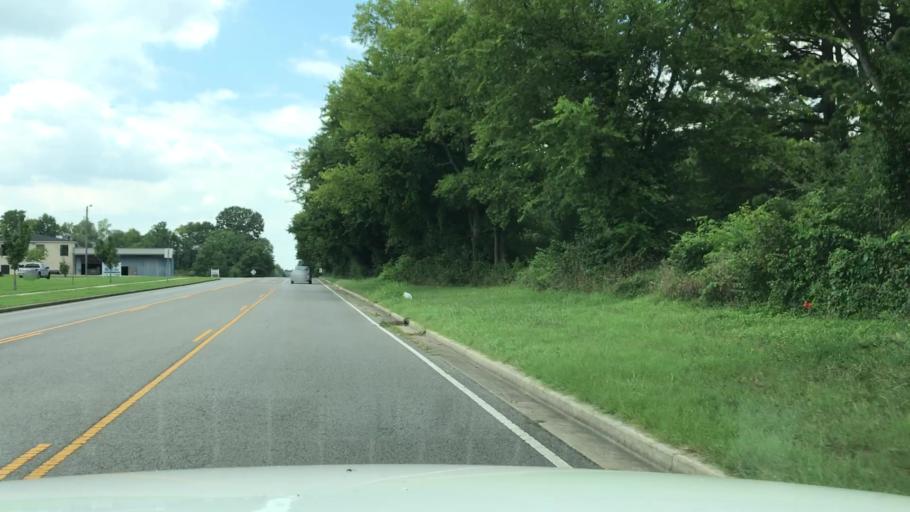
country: US
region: Tennessee
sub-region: Sumner County
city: Gallatin
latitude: 36.3839
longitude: -86.4645
